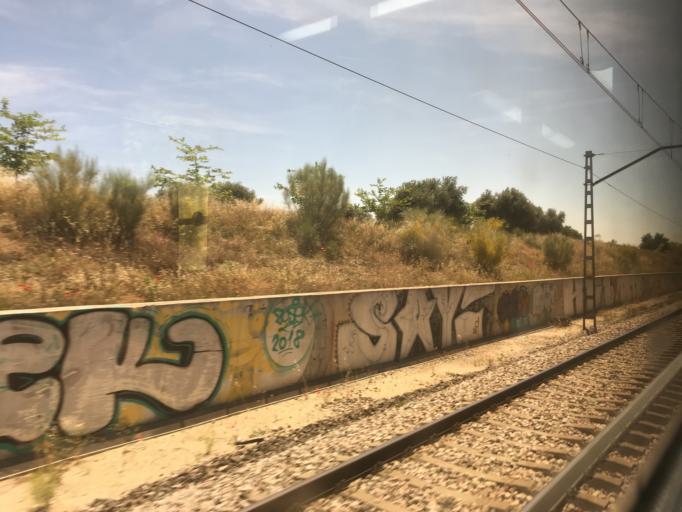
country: ES
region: Madrid
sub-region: Provincia de Madrid
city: Valdemoro
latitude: 40.2037
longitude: -3.6699
